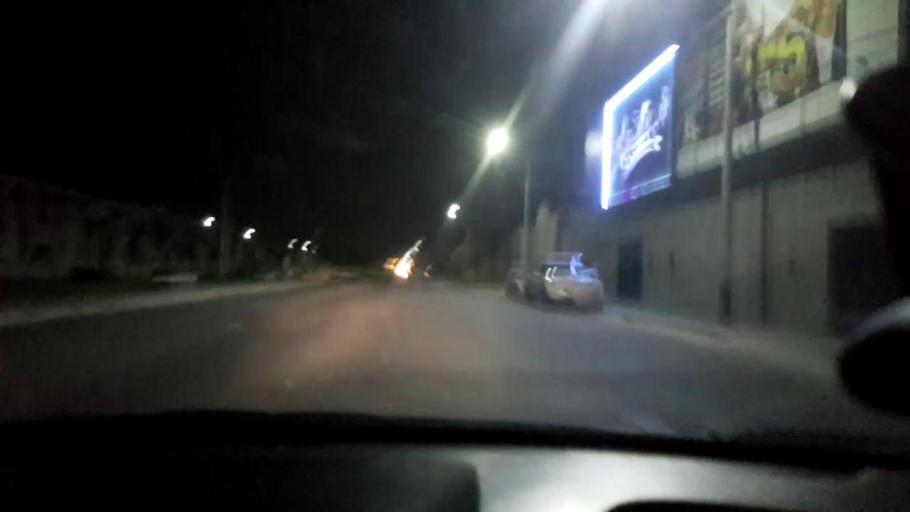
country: PE
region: Lambayeque
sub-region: Provincia de Chiclayo
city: Chiclayo
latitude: -6.7878
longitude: -79.8437
